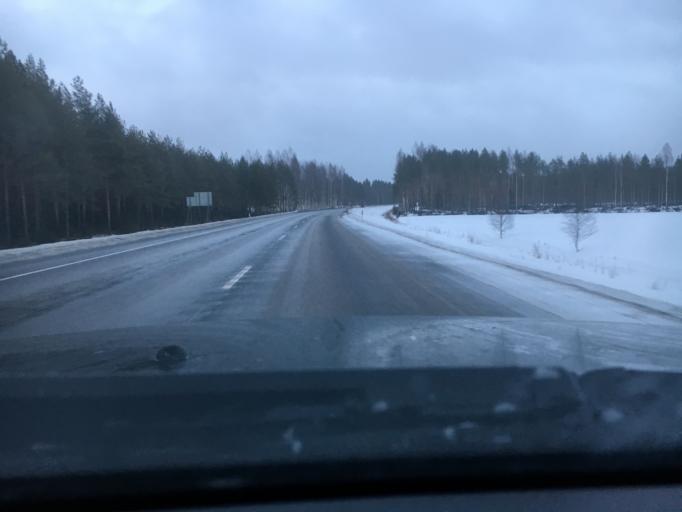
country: FI
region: Central Finland
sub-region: Jyvaeskylae
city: Hankasalmi
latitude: 62.3886
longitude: 26.6124
